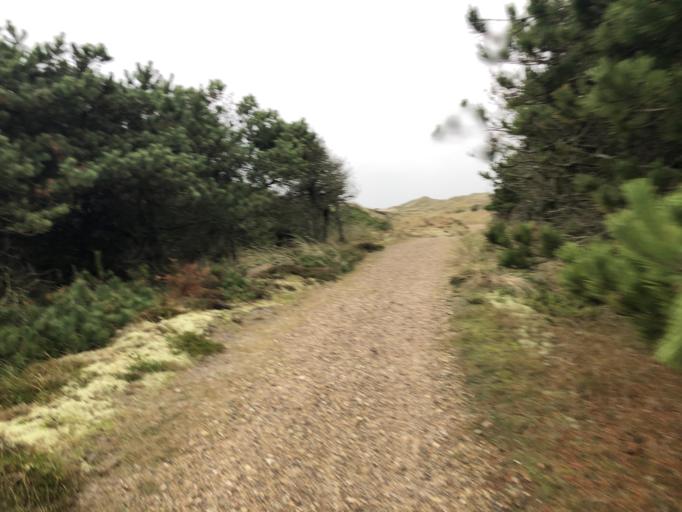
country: DK
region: Central Jutland
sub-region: Holstebro Kommune
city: Ulfborg
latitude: 56.2869
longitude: 8.1331
